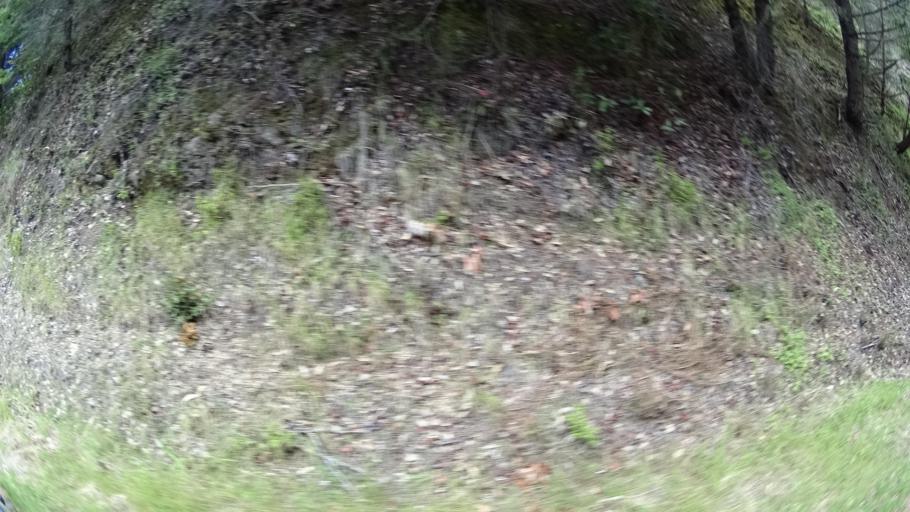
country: US
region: California
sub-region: Humboldt County
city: Blue Lake
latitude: 40.7634
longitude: -123.9269
